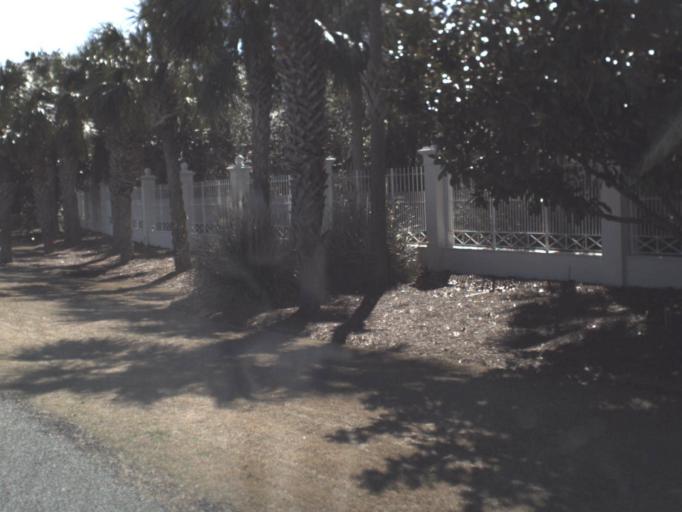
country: US
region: Florida
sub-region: Bay County
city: Laguna Beach
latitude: 30.2640
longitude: -85.9752
